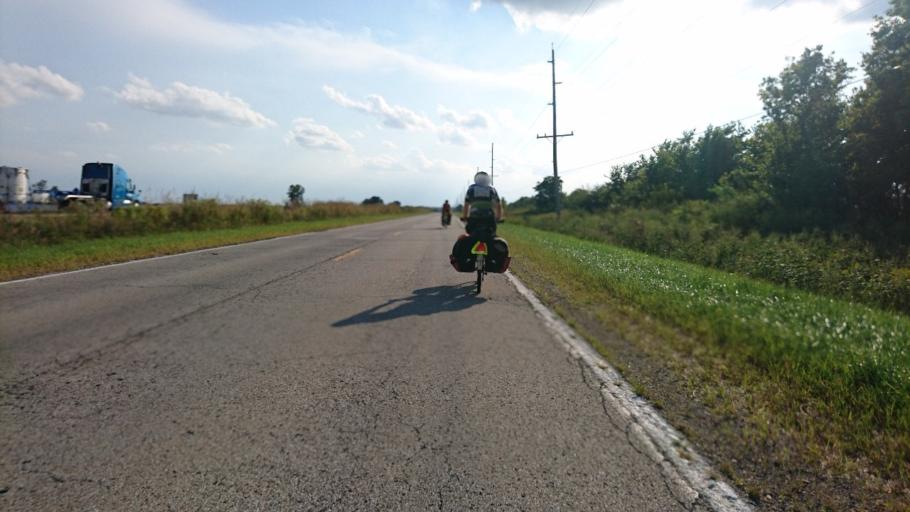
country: US
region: Illinois
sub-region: Logan County
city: Atlanta
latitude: 40.2971
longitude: -89.1897
